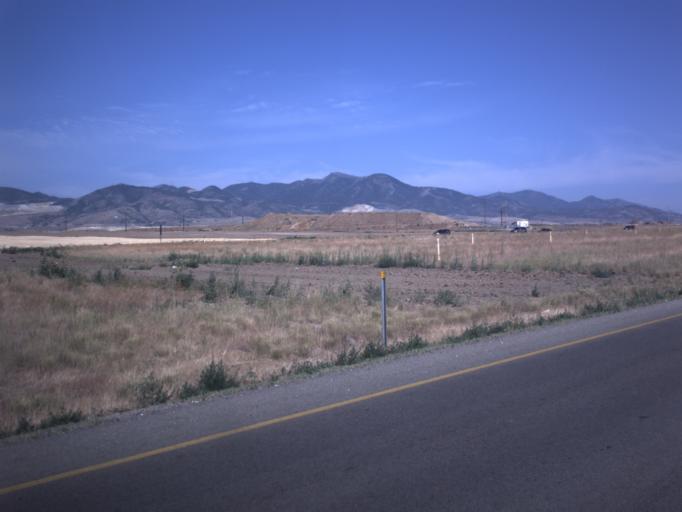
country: US
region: Utah
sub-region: Salt Lake County
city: Herriman
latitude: 40.5525
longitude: -112.0293
